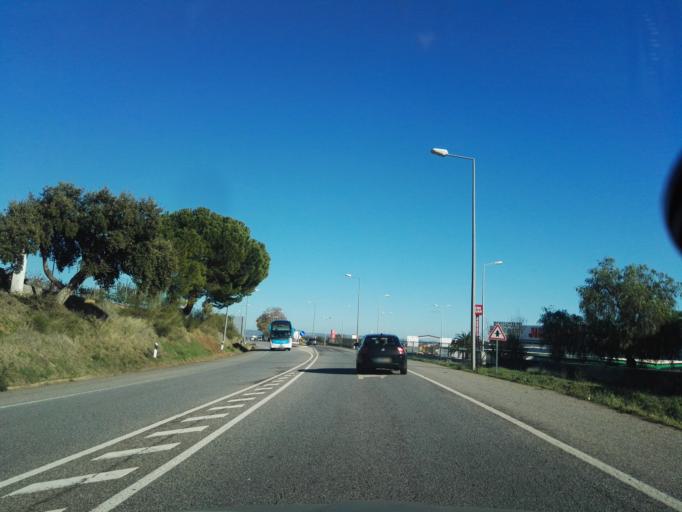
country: PT
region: Evora
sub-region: Borba
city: Borba
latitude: 38.8087
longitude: -7.4617
